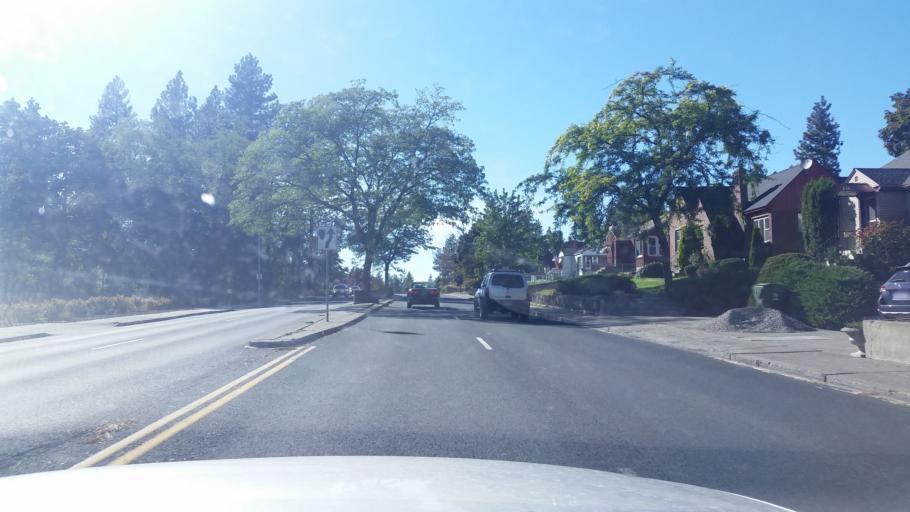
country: US
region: Washington
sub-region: Spokane County
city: Spokane
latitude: 47.6282
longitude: -117.3957
